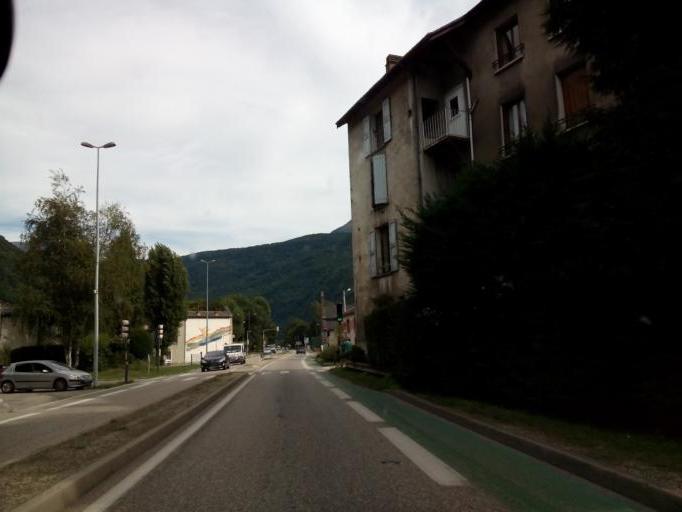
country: FR
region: Rhone-Alpes
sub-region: Departement de l'Isere
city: Notre-Dame-de-Mesage
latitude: 45.0579
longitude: 5.7702
